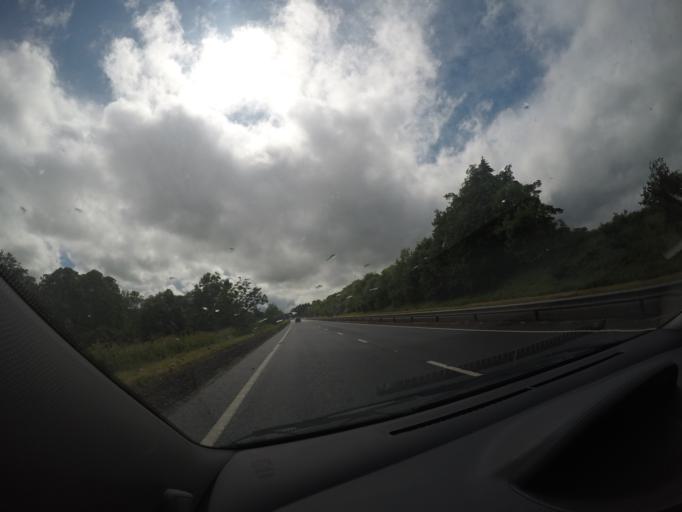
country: GB
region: Scotland
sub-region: Perth and Kinross
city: Auchterarder
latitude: 56.2916
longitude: -3.7014
